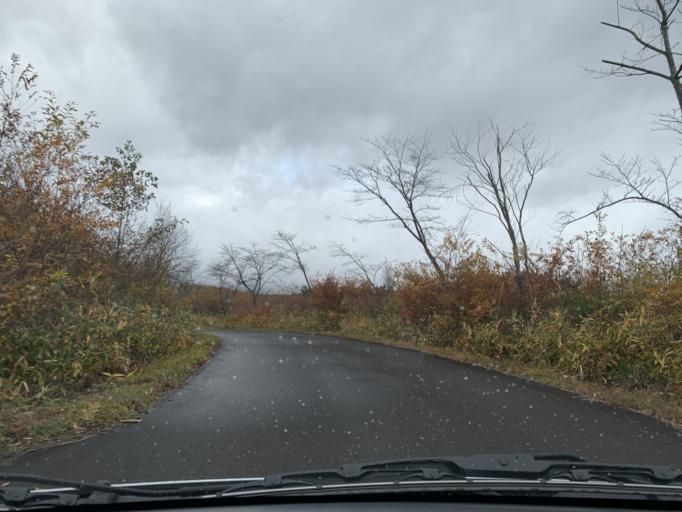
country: JP
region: Iwate
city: Mizusawa
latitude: 39.0816
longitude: 141.0198
